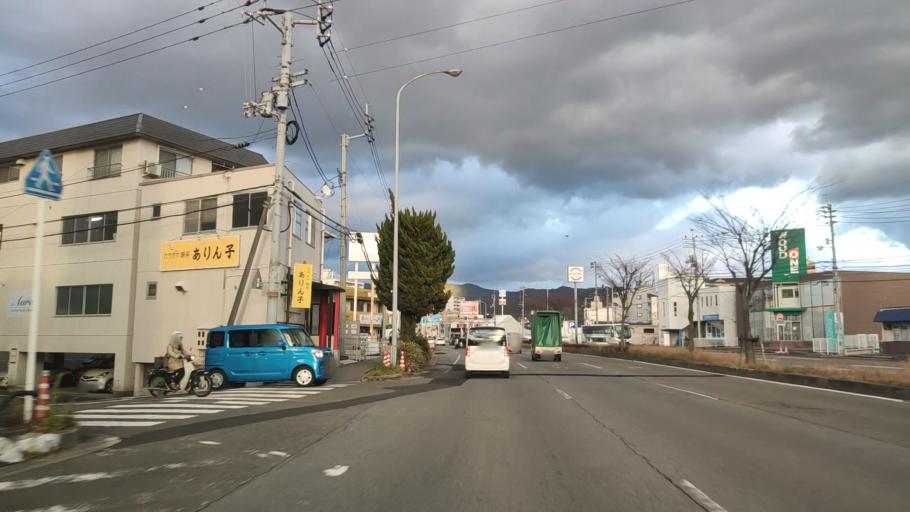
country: JP
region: Ehime
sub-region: Shikoku-chuo Shi
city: Matsuyama
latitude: 33.8229
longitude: 132.7772
